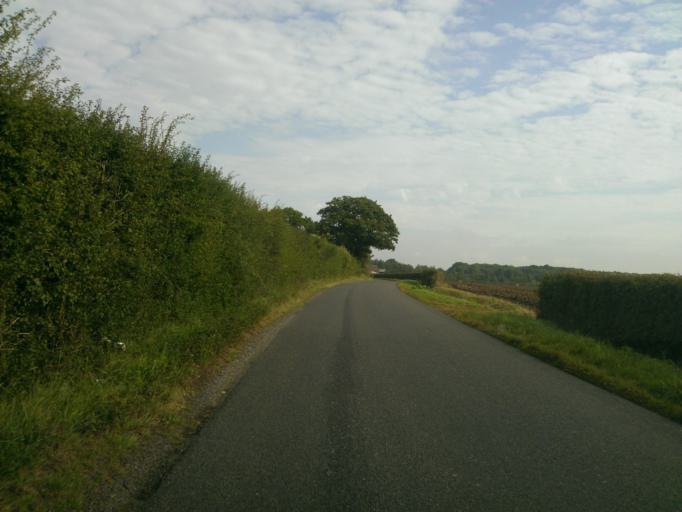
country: GB
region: England
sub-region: Essex
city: Saint Osyth
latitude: 51.8267
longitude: 1.1021
